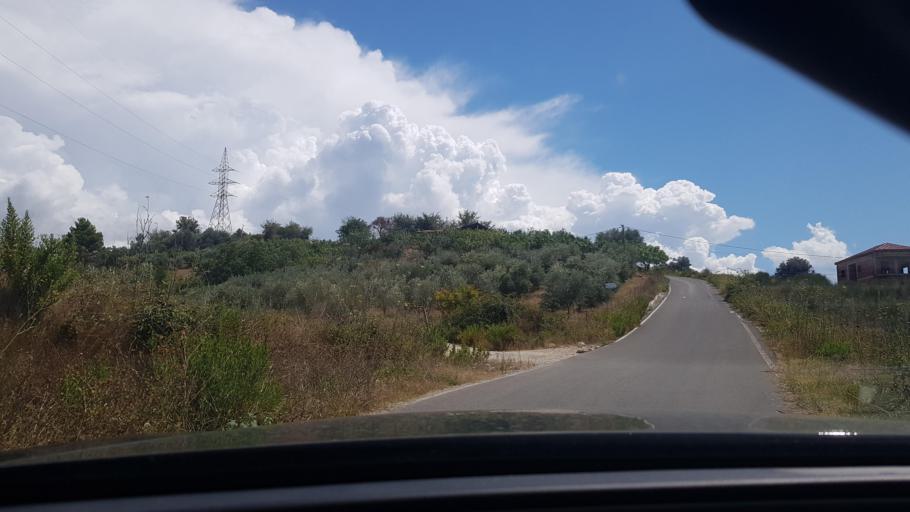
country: AL
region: Durres
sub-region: Rrethi i Durresit
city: Rrashbull
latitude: 41.2972
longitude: 19.5262
